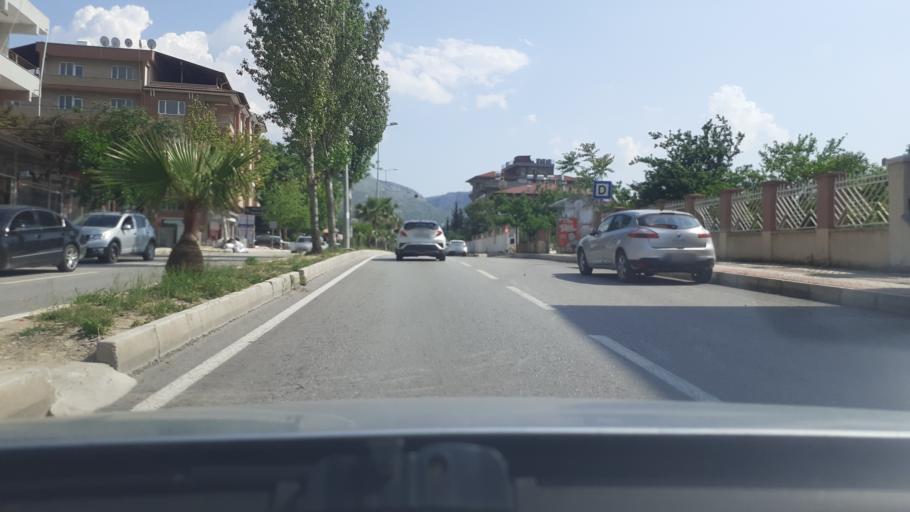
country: TR
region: Hatay
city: Gumusgoze
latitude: 36.1424
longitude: 36.1413
